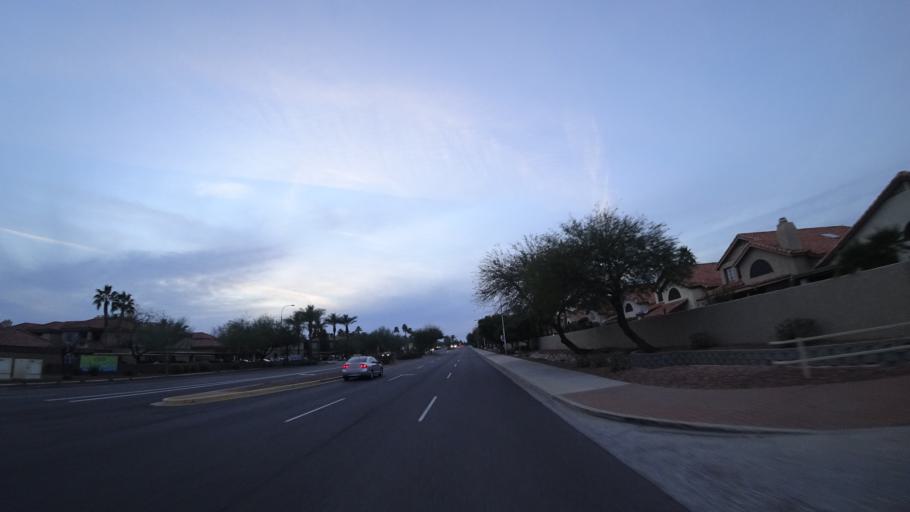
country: US
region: Arizona
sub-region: Maricopa County
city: Guadalupe
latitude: 33.3053
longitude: -112.0081
